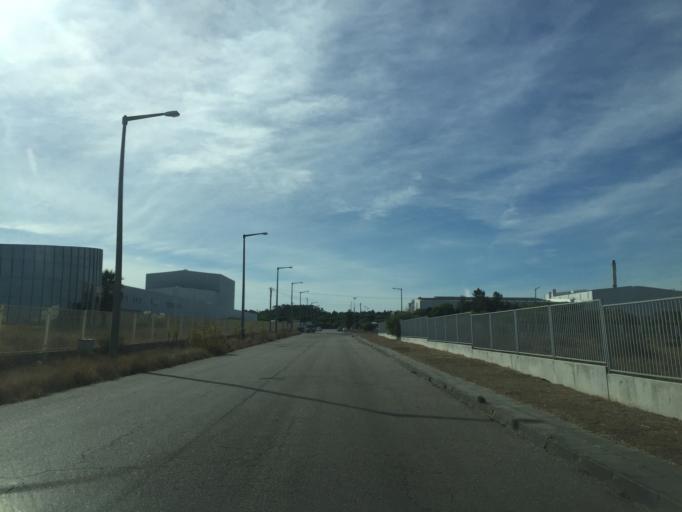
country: PT
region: Coimbra
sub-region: Figueira da Foz
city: Lavos
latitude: 40.1087
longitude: -8.8473
